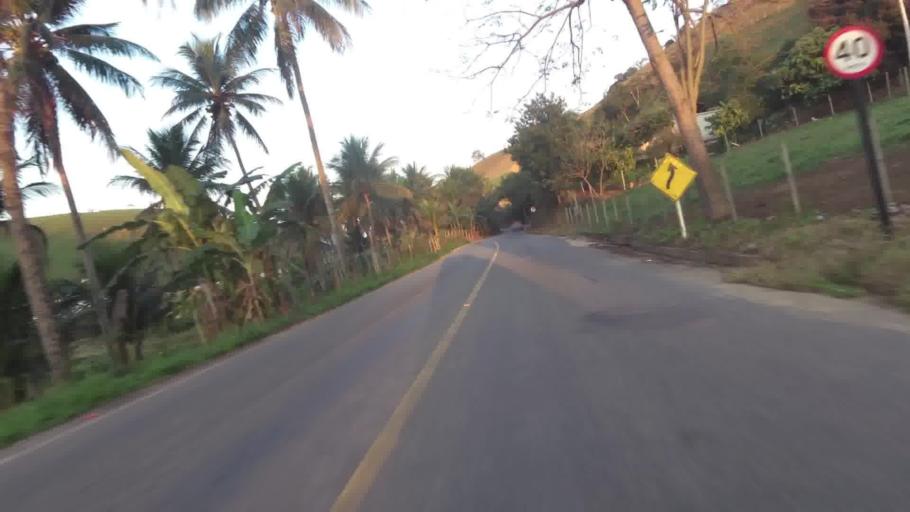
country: BR
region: Espirito Santo
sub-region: Alfredo Chaves
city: Alfredo Chaves
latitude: -20.6490
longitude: -40.6566
